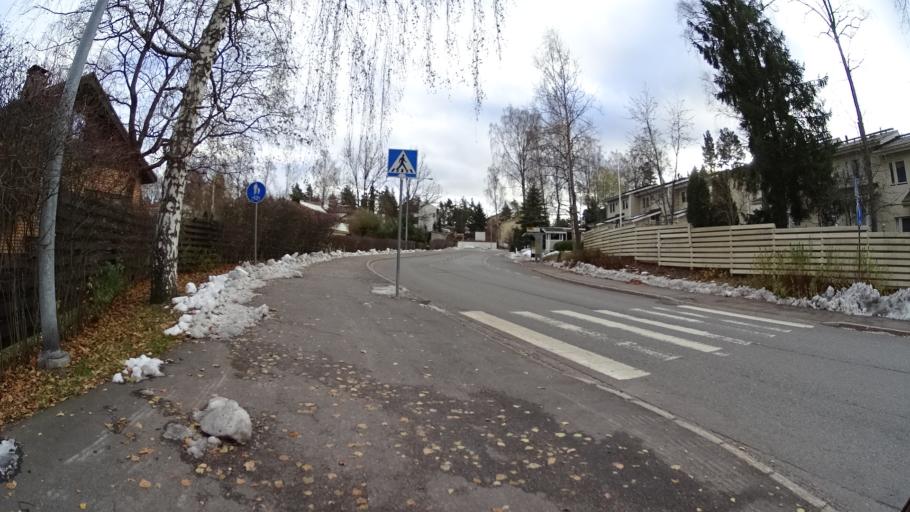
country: FI
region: Uusimaa
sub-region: Helsinki
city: Kilo
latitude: 60.2636
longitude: 24.8290
